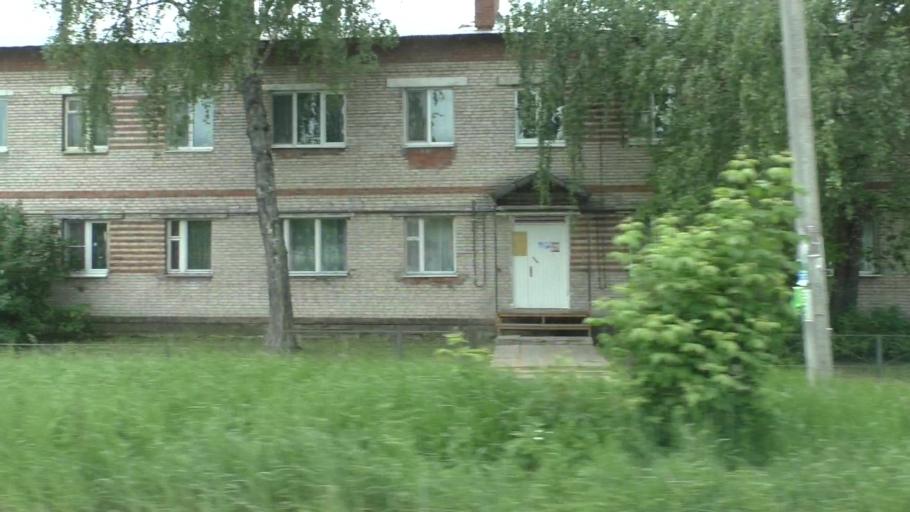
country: RU
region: Moskovskaya
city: Imeni Tsyurupy
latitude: 55.5060
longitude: 38.7725
